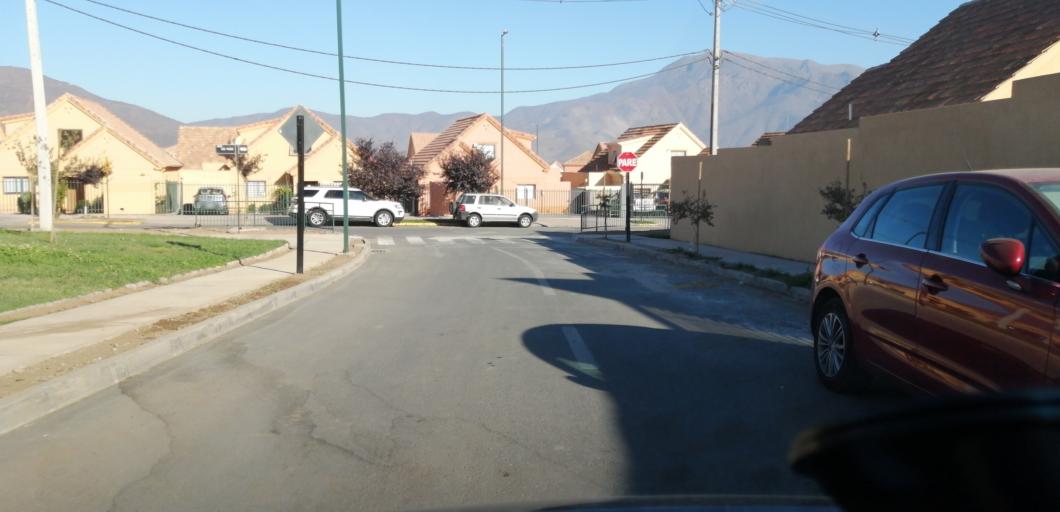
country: CL
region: Santiago Metropolitan
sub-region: Provincia de Santiago
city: Lo Prado
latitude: -33.4633
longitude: -70.8549
